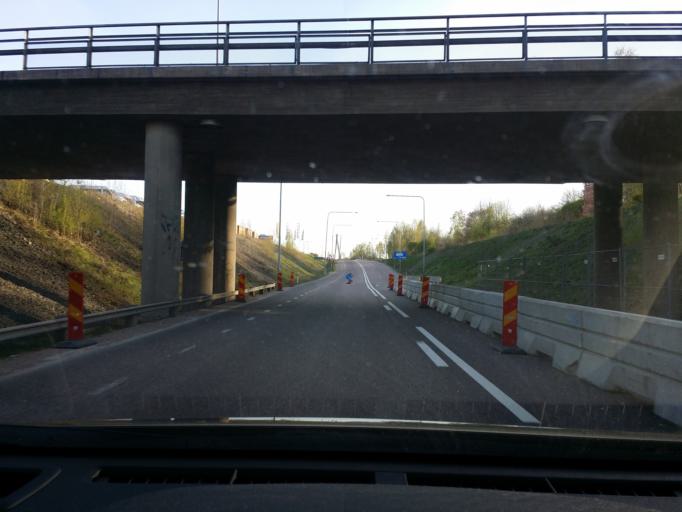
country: SE
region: Dalarna
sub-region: Avesta Kommun
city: Avesta
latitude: 60.1436
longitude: 16.1950
